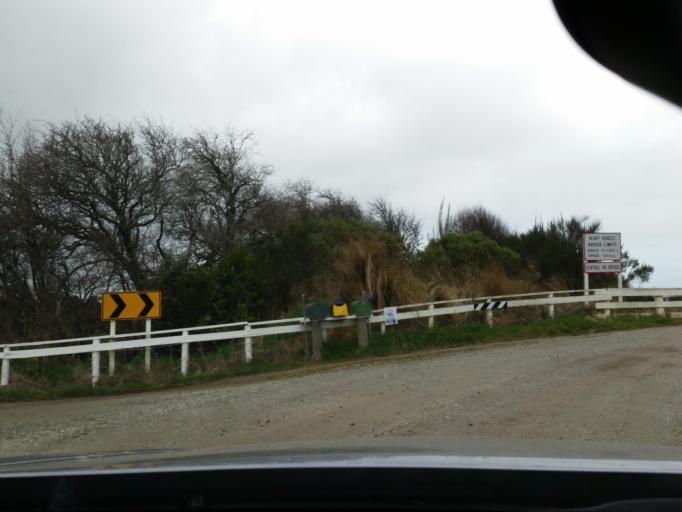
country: NZ
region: Southland
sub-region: Southland District
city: Winton
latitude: -46.2419
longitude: 168.4778
